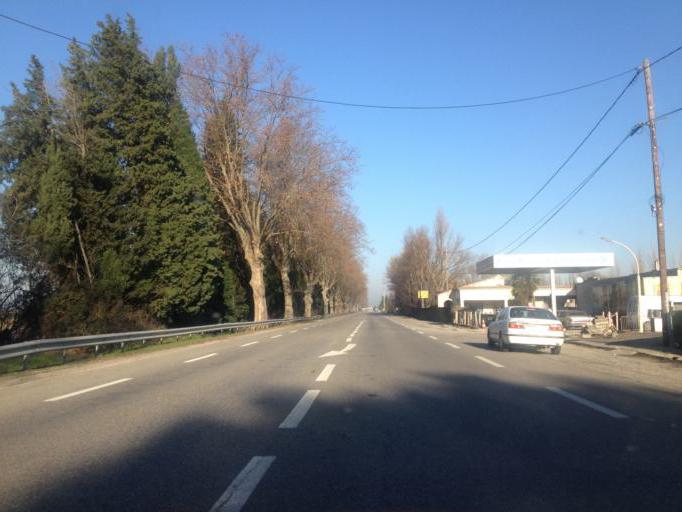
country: FR
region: Provence-Alpes-Cote d'Azur
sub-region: Departement du Vaucluse
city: Mondragon
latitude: 44.2617
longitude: 4.7050
